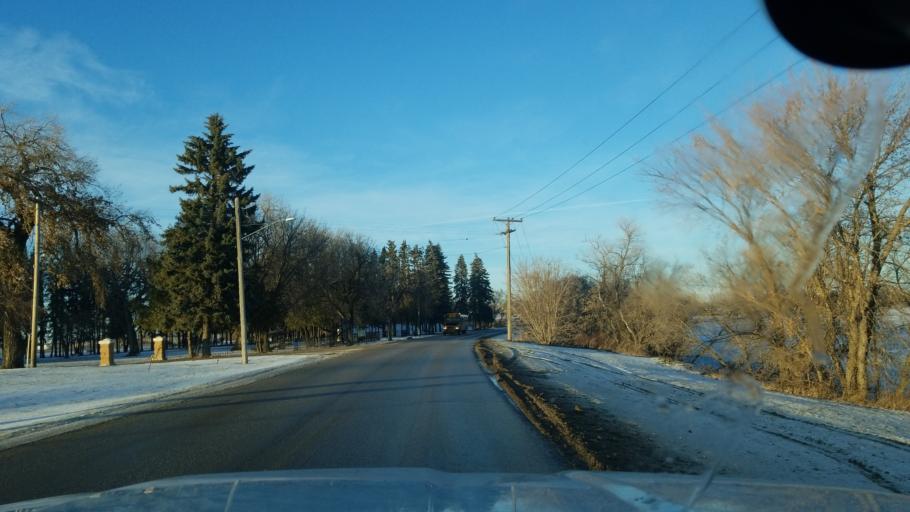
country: CA
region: Manitoba
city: Portage la Prairie
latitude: 49.9616
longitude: -98.3217
